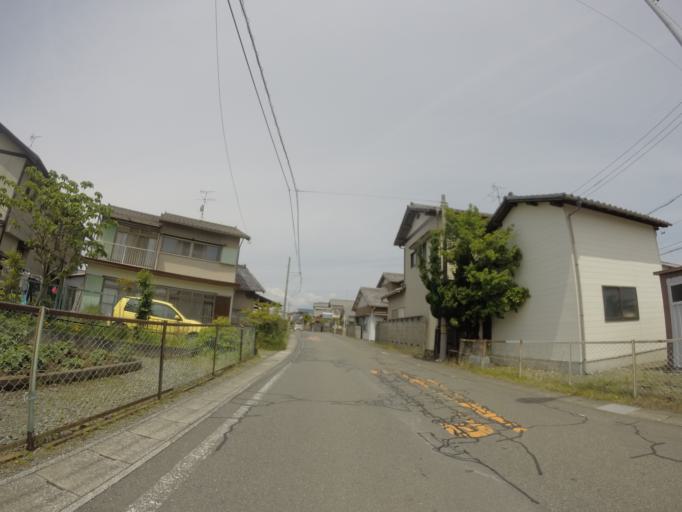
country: JP
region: Shizuoka
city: Yaizu
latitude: 34.8436
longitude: 138.3292
